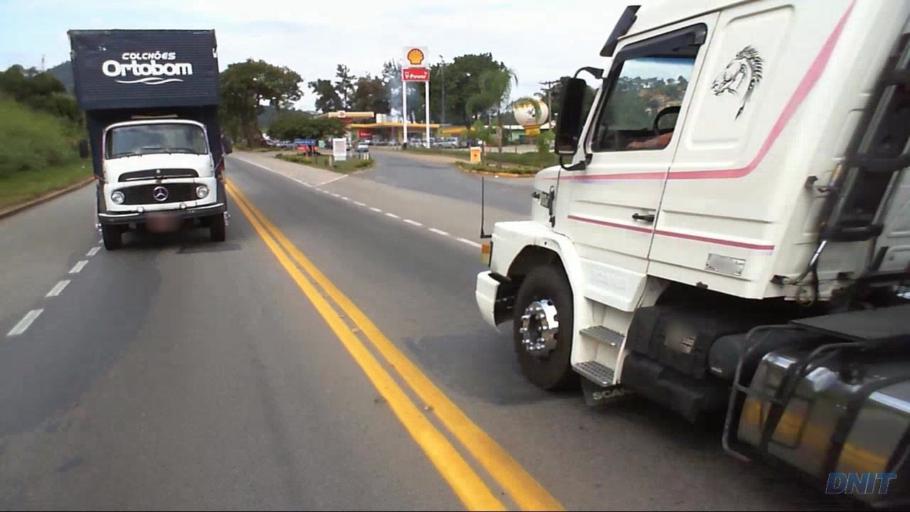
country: BR
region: Minas Gerais
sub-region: Santa Luzia
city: Santa Luzia
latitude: -19.8397
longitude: -43.8773
